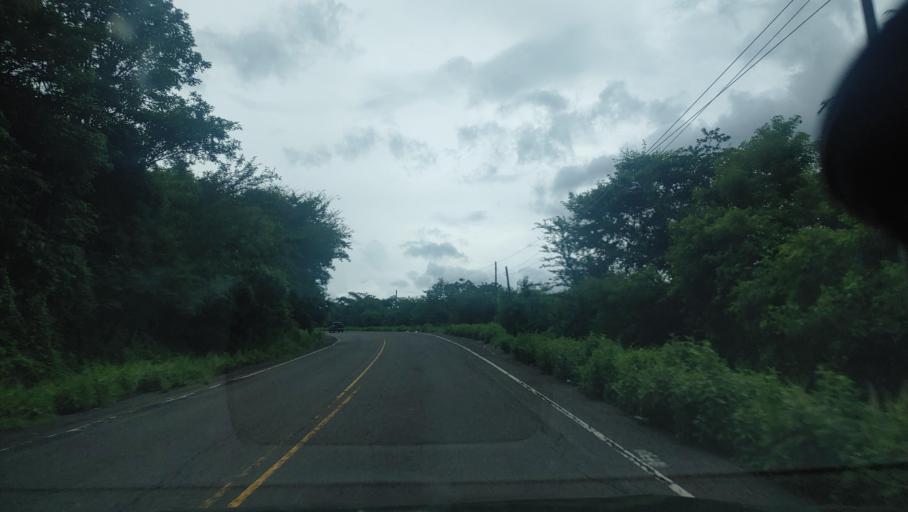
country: HN
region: Choluteca
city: Santa Ana de Yusguare
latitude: 13.3684
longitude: -87.0777
